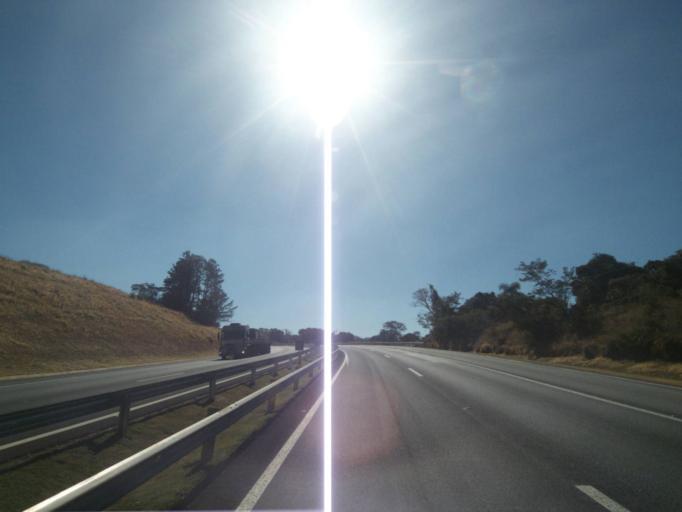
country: BR
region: Parana
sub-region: Carambei
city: Carambei
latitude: -24.8741
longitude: -50.4434
